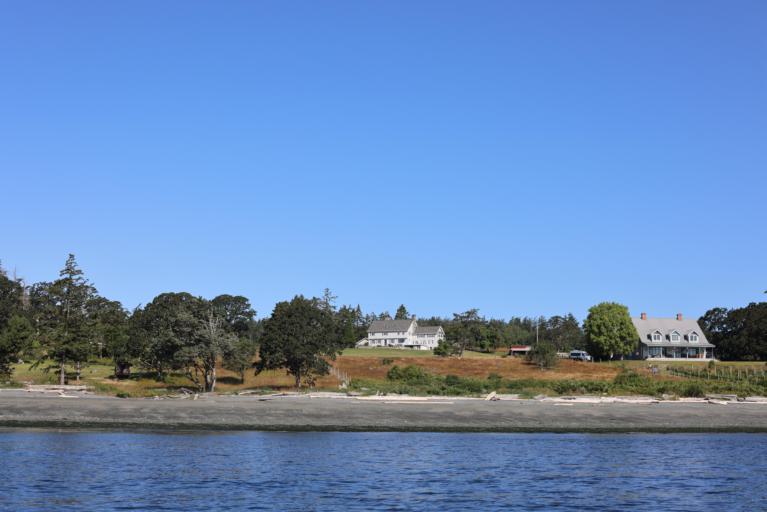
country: CA
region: British Columbia
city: Metchosin
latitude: 48.3646
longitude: -123.5311
